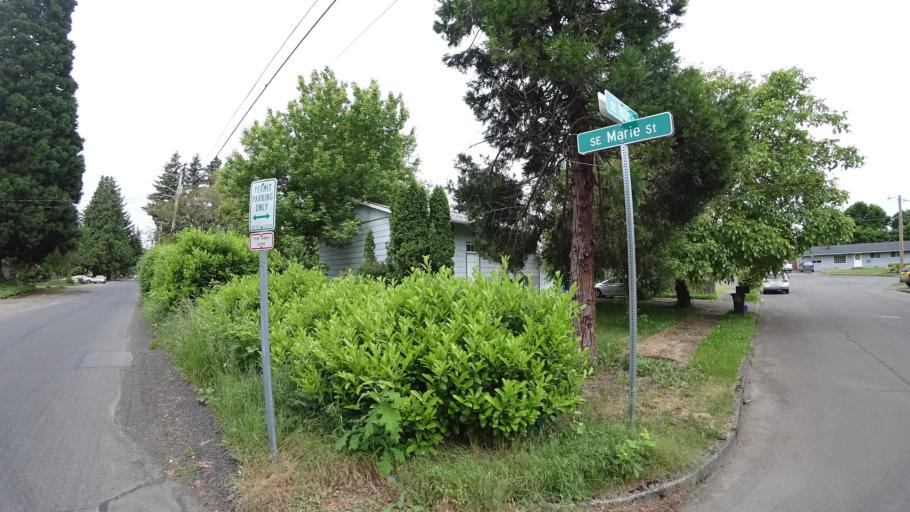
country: US
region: Oregon
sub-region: Multnomah County
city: Gresham
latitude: 45.4945
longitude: -122.4772
